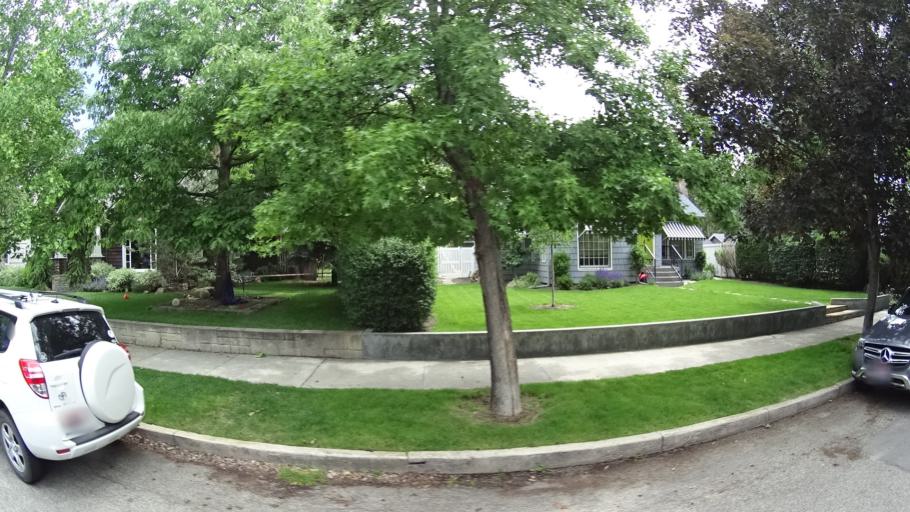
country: US
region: Idaho
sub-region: Ada County
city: Boise
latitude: 43.6297
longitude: -116.2169
